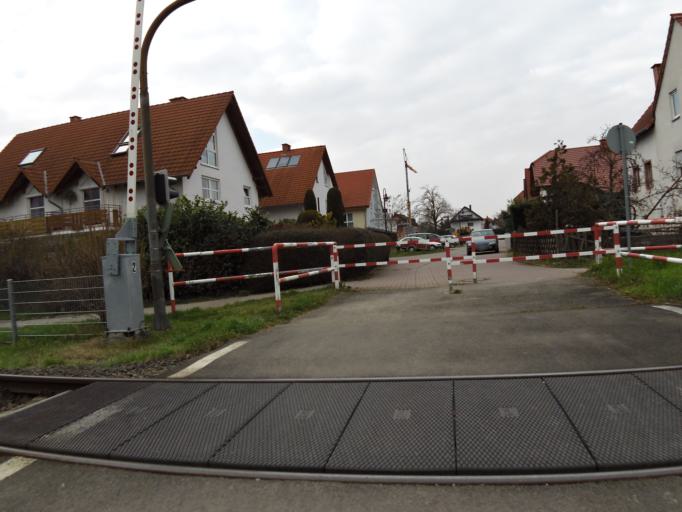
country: DE
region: Rheinland-Pfalz
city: Lambsheim
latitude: 49.5114
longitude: 8.2909
